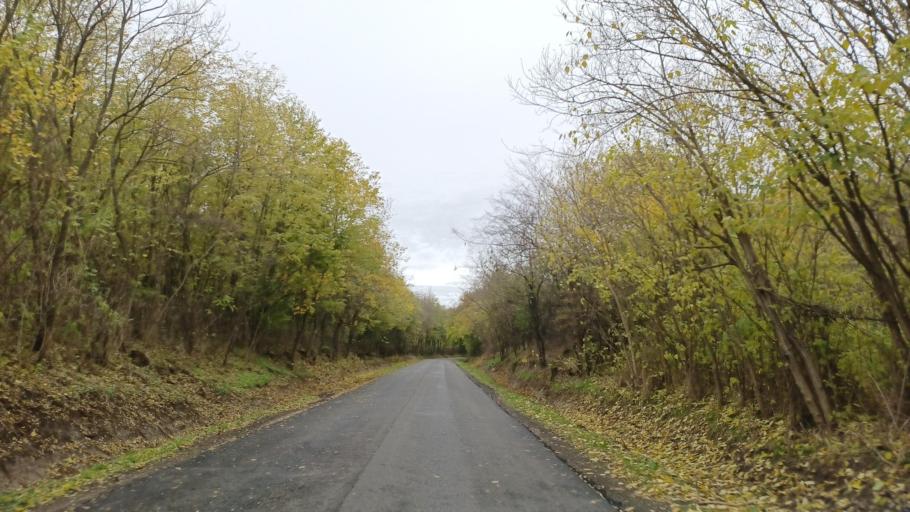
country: HU
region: Tolna
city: Tengelic
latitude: 46.5319
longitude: 18.7628
